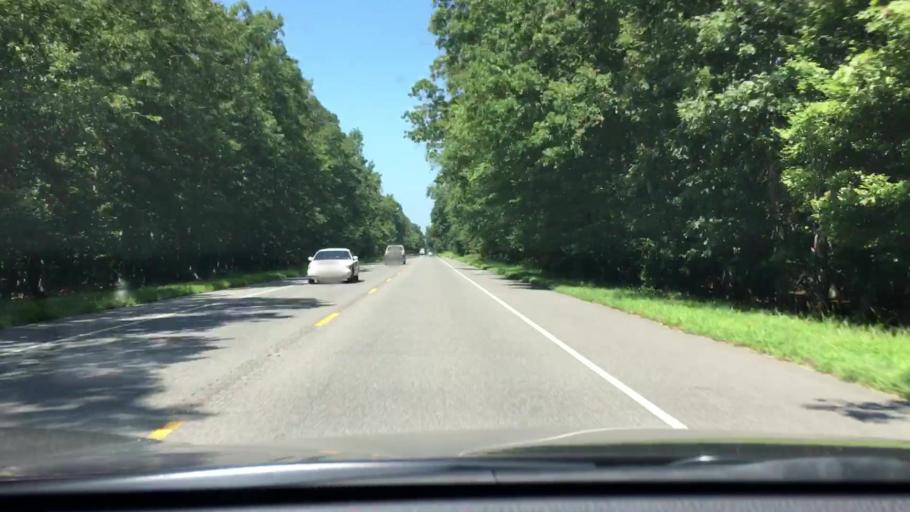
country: US
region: New Jersey
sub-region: Cumberland County
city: Laurel Lake
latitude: 39.3451
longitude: -75.0420
